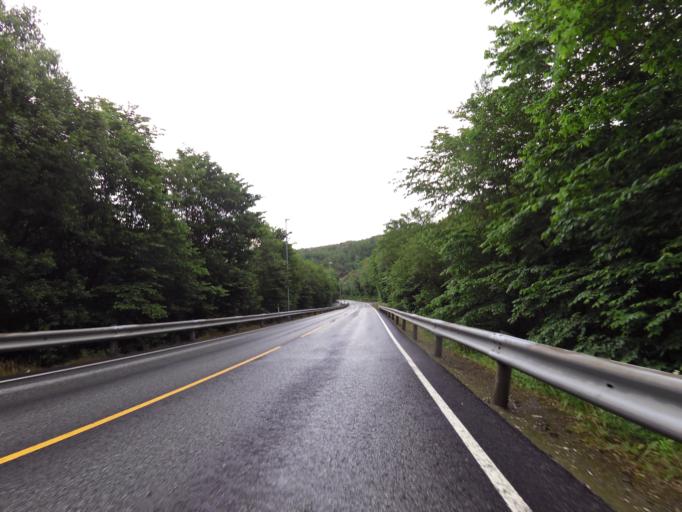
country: NO
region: Vest-Agder
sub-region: Farsund
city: Farsund
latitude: 58.1023
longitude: 6.8974
